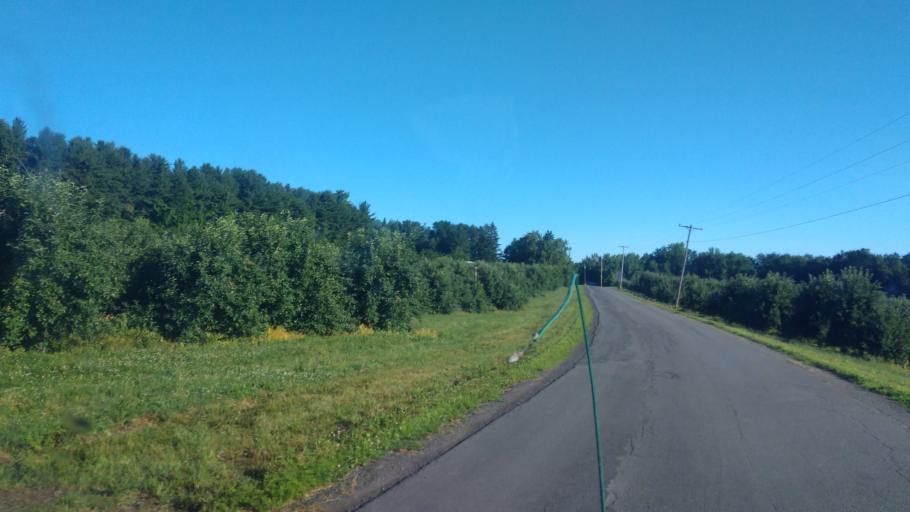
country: US
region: New York
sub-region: Wayne County
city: Sodus
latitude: 43.1855
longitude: -77.0618
